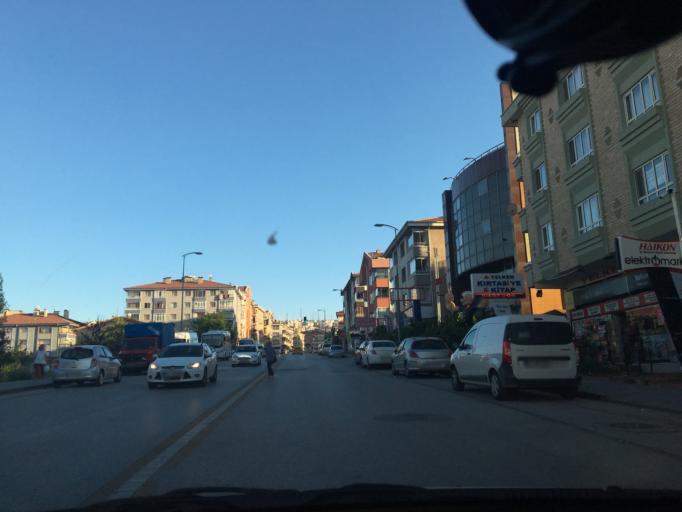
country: TR
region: Ankara
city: Ankara
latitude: 39.8888
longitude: 32.8290
